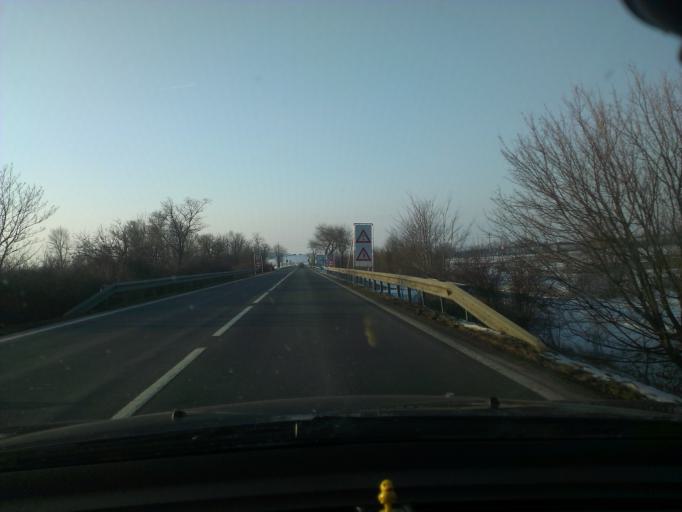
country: AT
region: Burgenland
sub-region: Eisenstadt-Umgebung
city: Donnerskirchen
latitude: 47.8729
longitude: 16.6487
